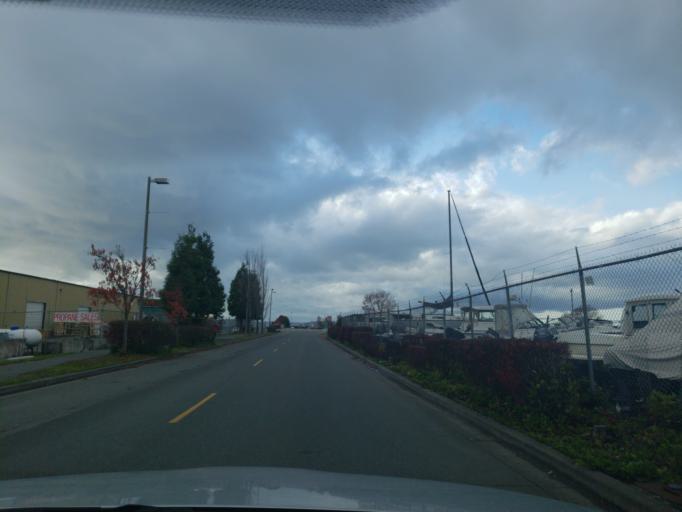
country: US
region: Washington
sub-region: Snohomish County
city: Everett
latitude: 48.0043
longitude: -122.2159
